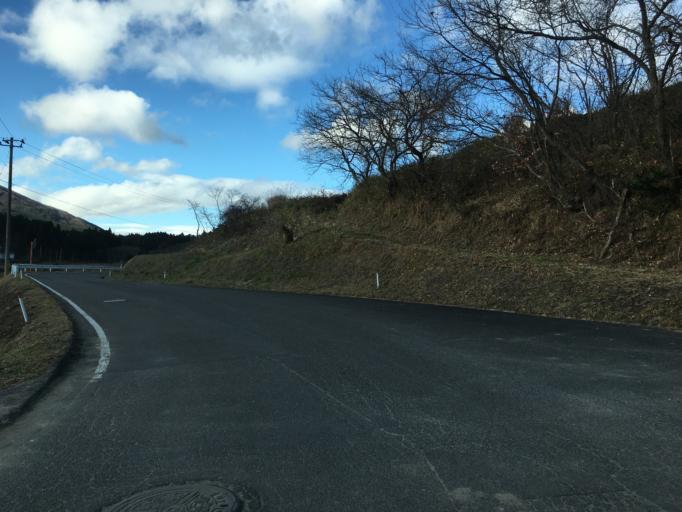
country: JP
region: Fukushima
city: Ishikawa
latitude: 37.2600
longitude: 140.5644
